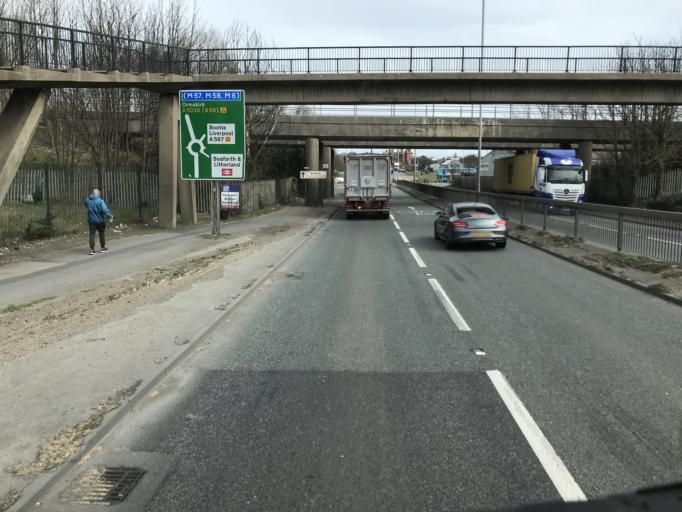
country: GB
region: England
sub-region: Sefton
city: Bootle
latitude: 53.4666
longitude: -3.0072
